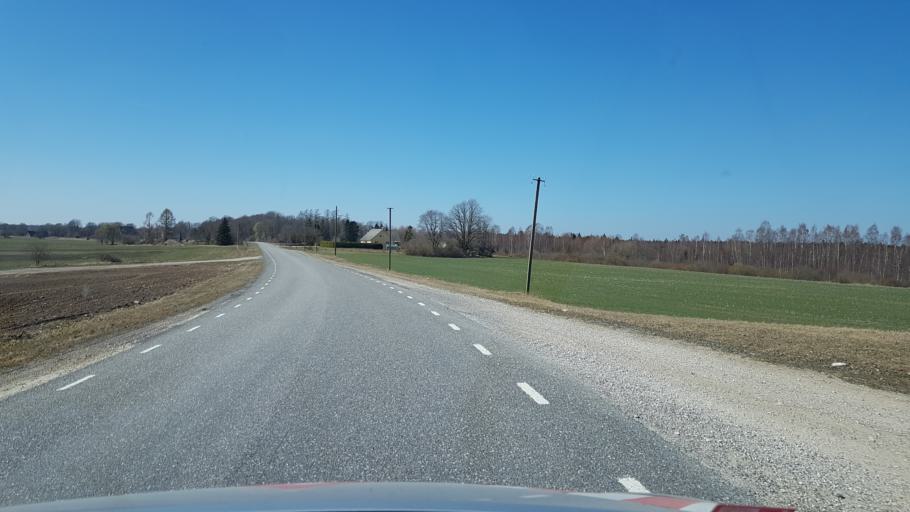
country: EE
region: Jaervamaa
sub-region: Koeru vald
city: Koeru
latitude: 59.0085
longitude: 26.1271
